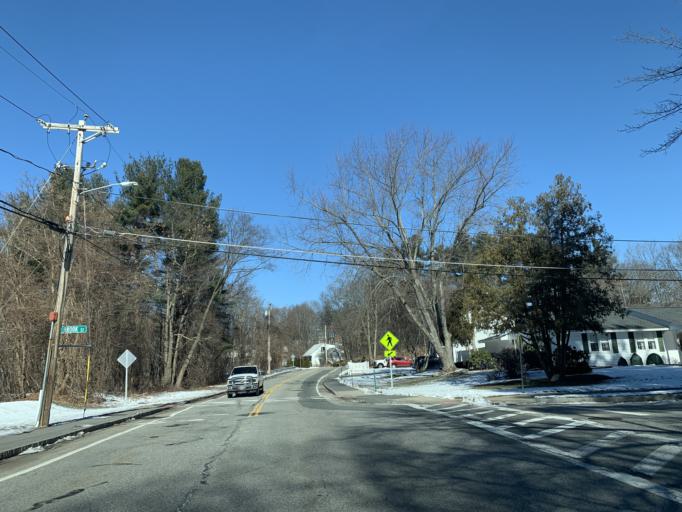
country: US
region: Massachusetts
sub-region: Middlesex County
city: Chelmsford
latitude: 42.5953
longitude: -71.3464
